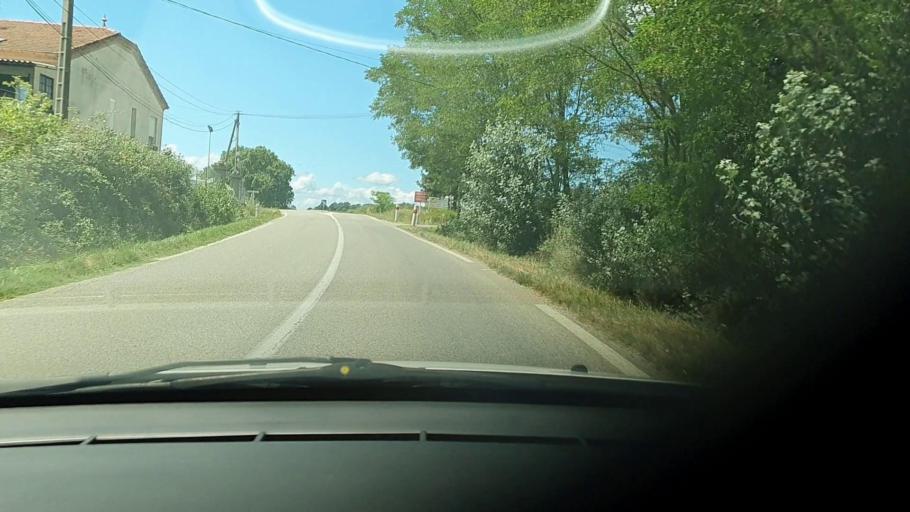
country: FR
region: Languedoc-Roussillon
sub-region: Departement du Gard
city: Saint-Chaptes
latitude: 44.0548
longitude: 4.2847
